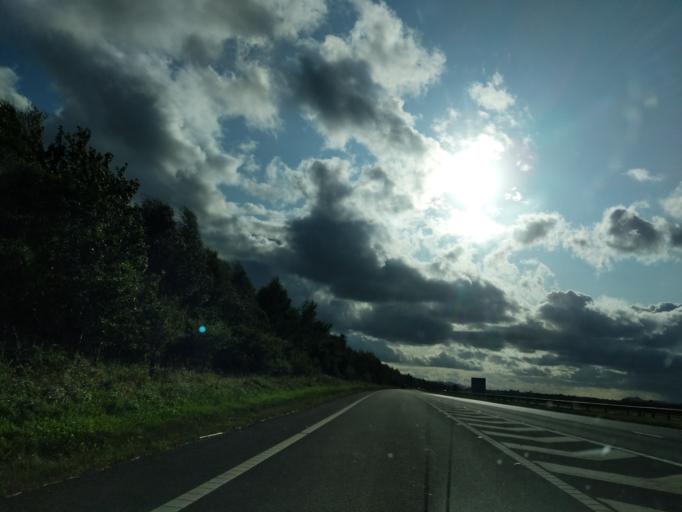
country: GB
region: Scotland
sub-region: East Lothian
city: Macmerry
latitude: 55.9490
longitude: -2.8854
